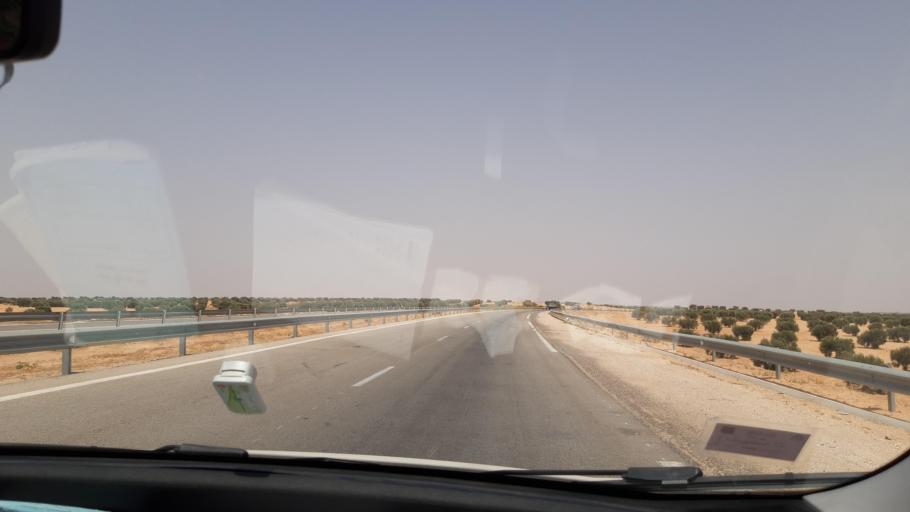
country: TN
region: Safaqis
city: Bi'r `Ali Bin Khalifah
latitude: 34.5223
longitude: 10.0801
